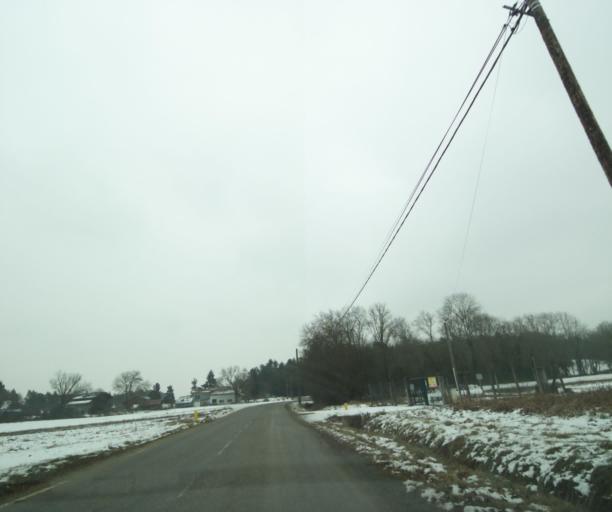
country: FR
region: Rhone-Alpes
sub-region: Departement de la Haute-Savoie
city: Reignier-Esery
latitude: 46.1252
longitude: 6.2821
